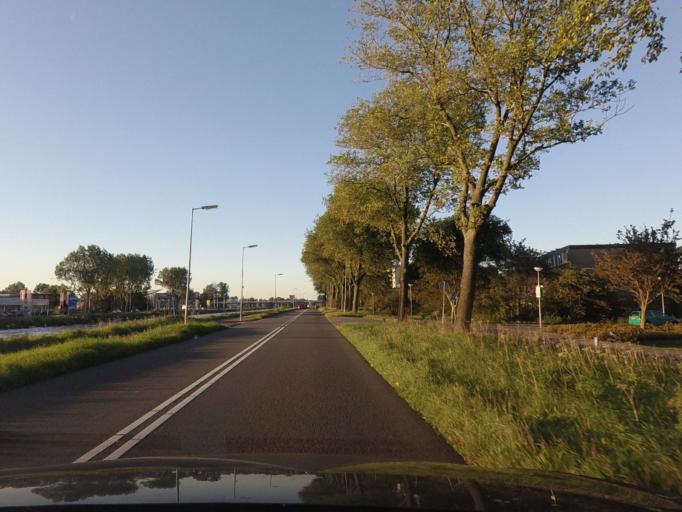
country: NL
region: North Holland
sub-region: Gemeente Alkmaar
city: Alkmaar
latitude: 52.6427
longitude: 4.7456
